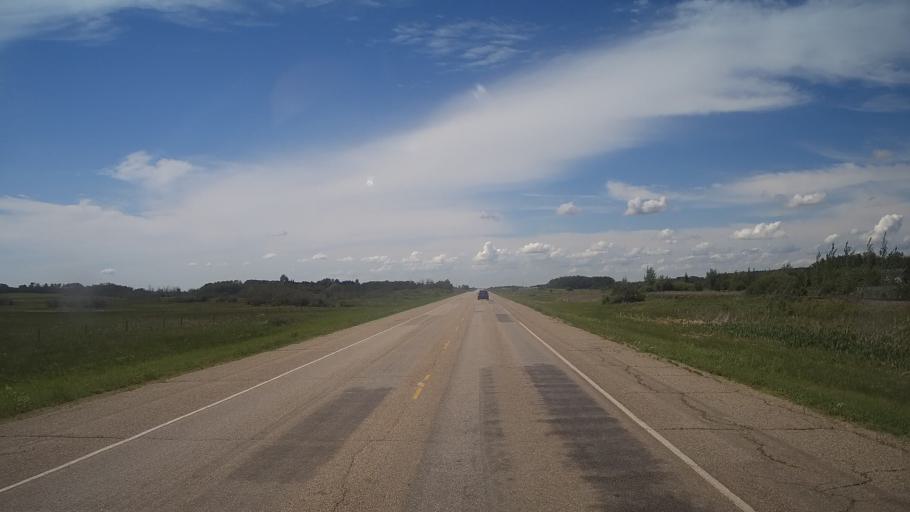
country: CA
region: Saskatchewan
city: Yorkton
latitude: 51.0607
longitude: -102.2046
